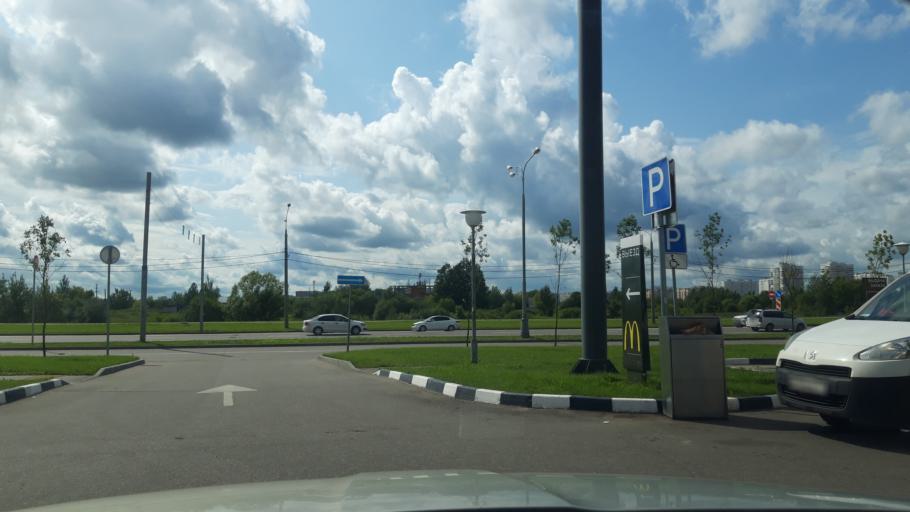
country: RU
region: Moscow
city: Zelenograd
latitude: 55.9647
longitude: 37.1865
